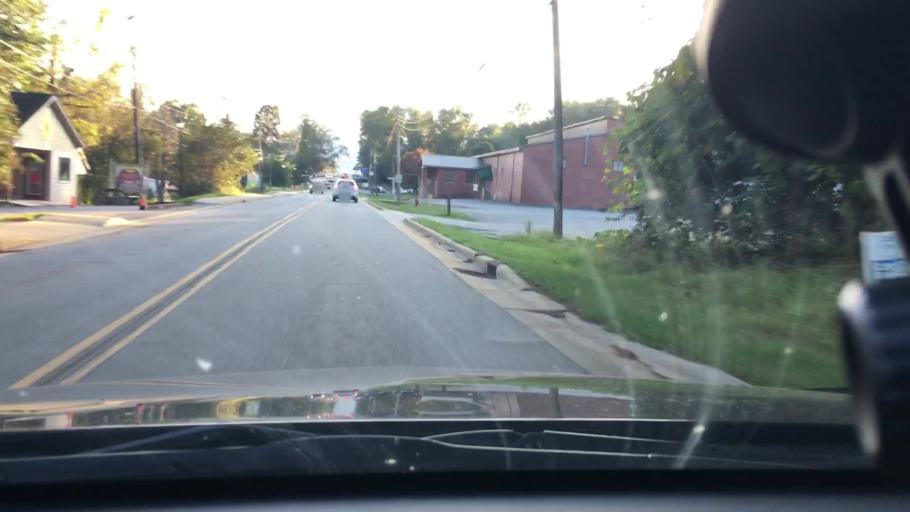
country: US
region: North Carolina
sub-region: Polk County
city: Columbus
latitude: 35.2555
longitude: -82.1946
